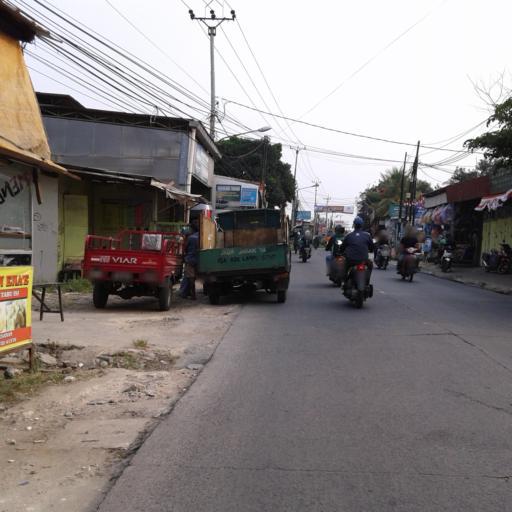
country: ID
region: West Java
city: Sawangan
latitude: -6.3646
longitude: 106.7755
